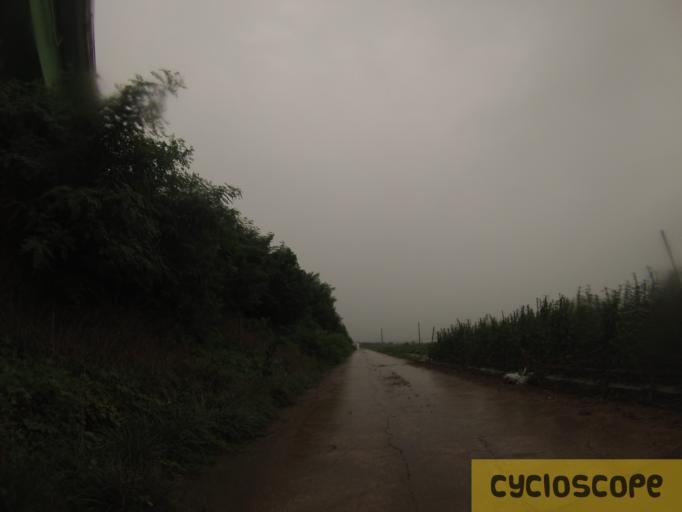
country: KR
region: Jeollabuk-do
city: Kunsan
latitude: 36.1047
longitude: 126.6102
